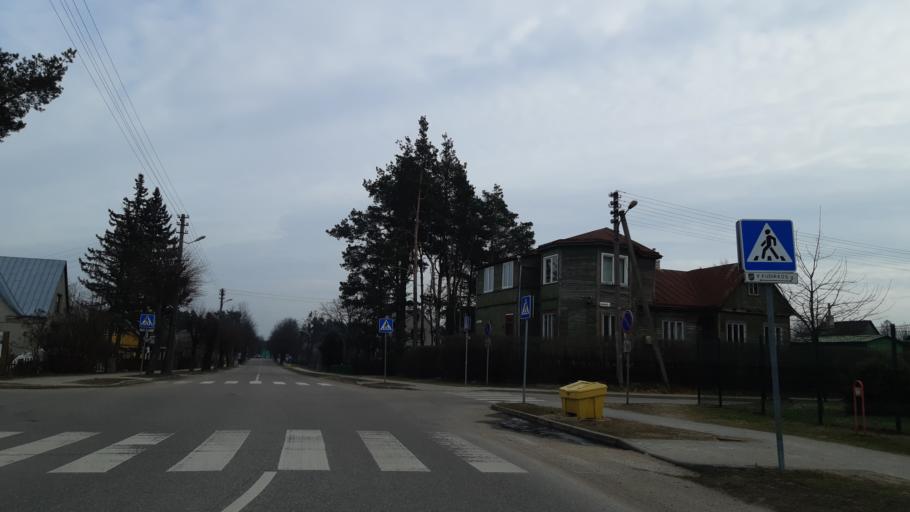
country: LT
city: Kazlu Ruda
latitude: 54.7539
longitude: 23.4967
